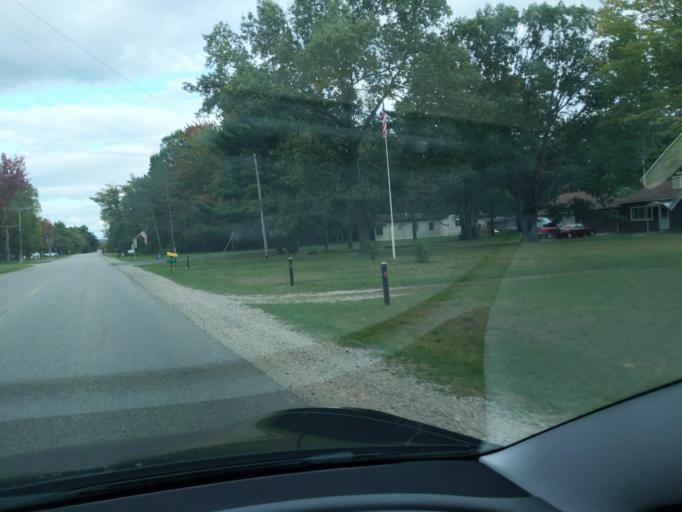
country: US
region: Michigan
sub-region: Kalkaska County
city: Rapid City
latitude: 44.8398
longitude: -85.2971
